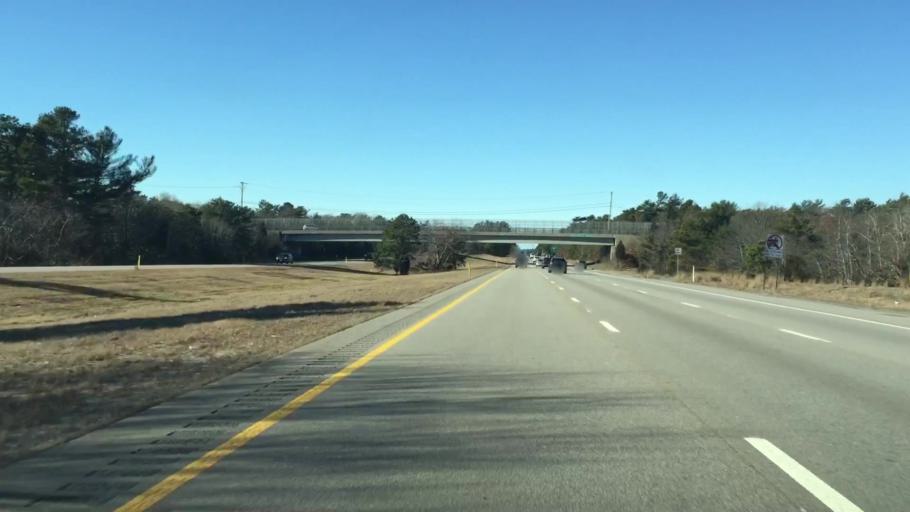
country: US
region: Massachusetts
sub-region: Plymouth County
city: Onset
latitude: 41.7673
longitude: -70.6782
